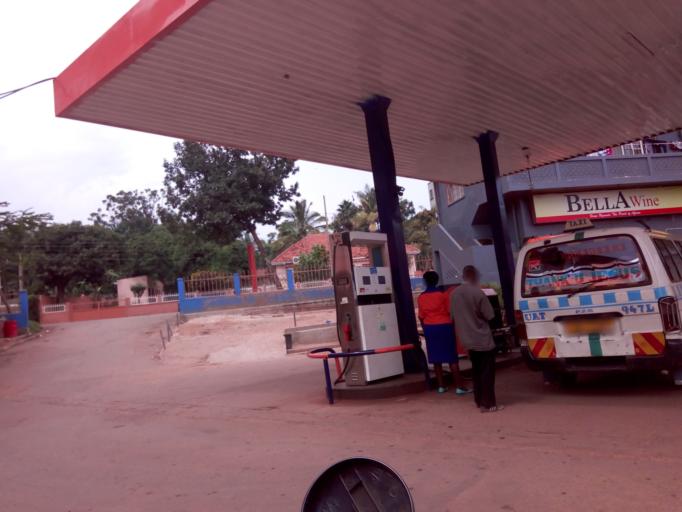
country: UG
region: Central Region
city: Kampala Central Division
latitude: 0.3290
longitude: 32.5746
